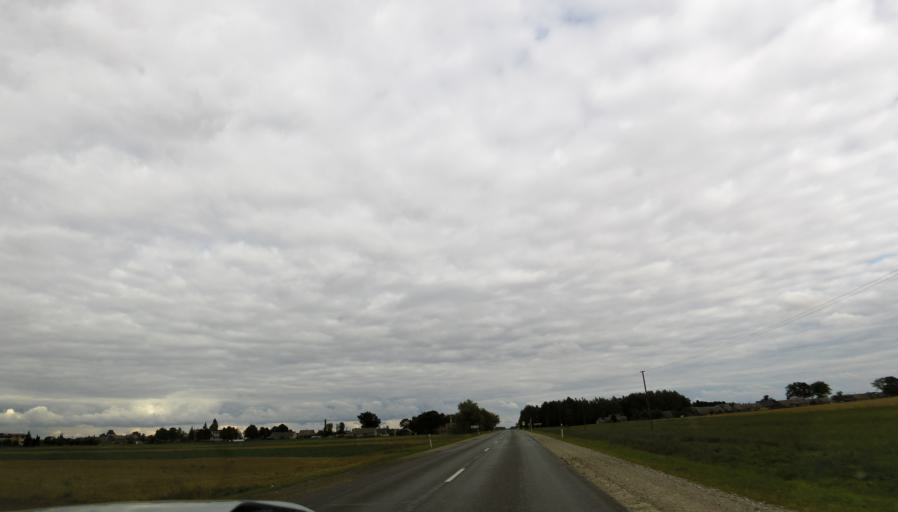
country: LT
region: Panevezys
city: Pasvalys
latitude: 56.0156
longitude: 24.2003
